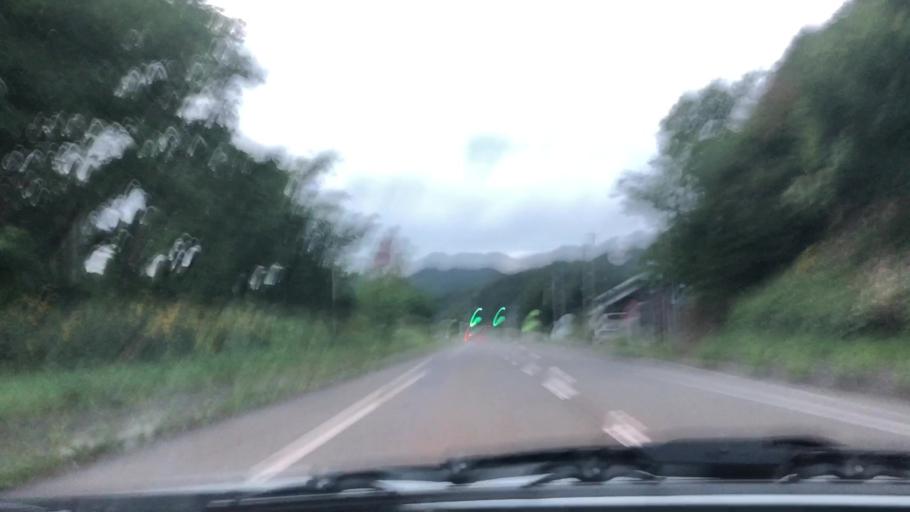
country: JP
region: Hokkaido
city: Chitose
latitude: 42.9093
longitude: 141.9790
